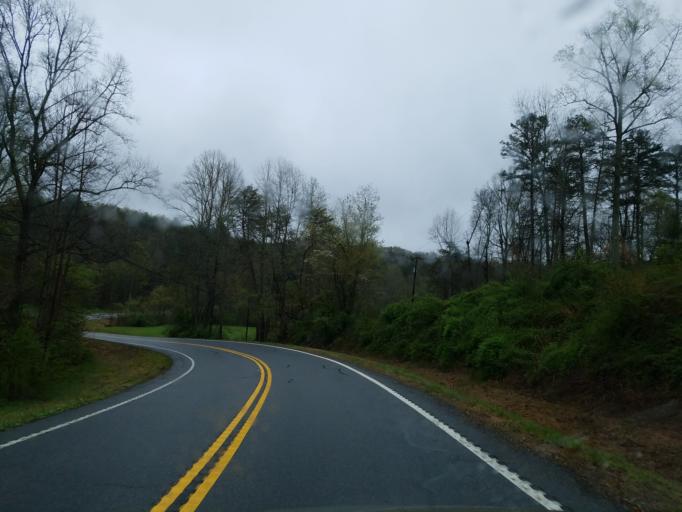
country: US
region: Georgia
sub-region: Fannin County
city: Blue Ridge
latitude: 34.8639
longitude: -84.2315
